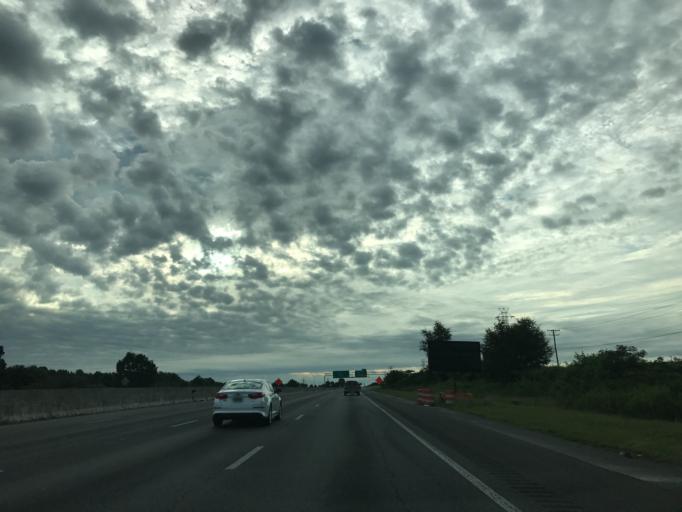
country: US
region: South Carolina
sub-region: Spartanburg County
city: Fairforest
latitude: 34.9632
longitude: -82.0420
